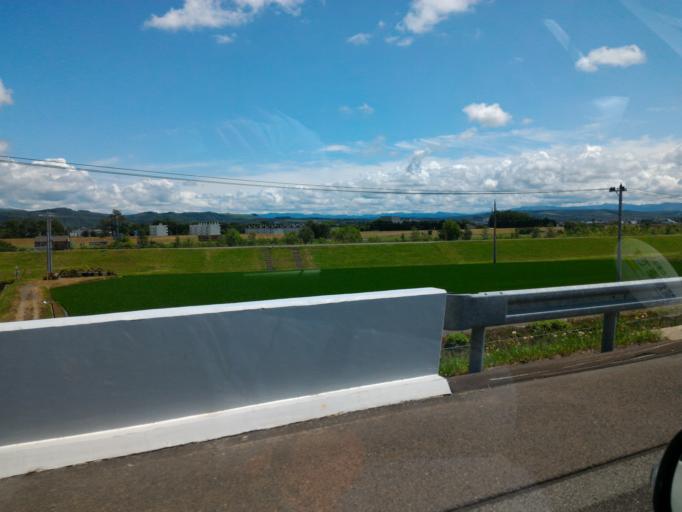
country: JP
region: Hokkaido
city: Nayoro
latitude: 44.3563
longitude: 142.4358
